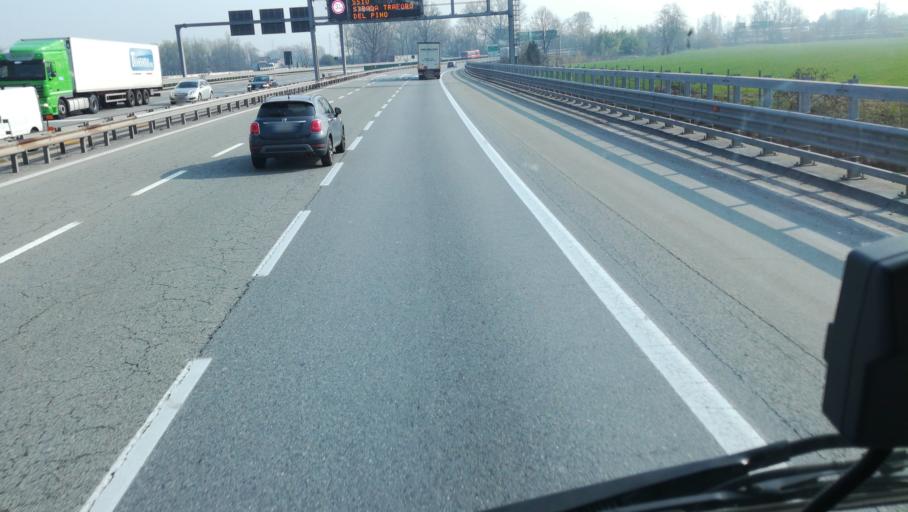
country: IT
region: Piedmont
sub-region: Provincia di Torino
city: Settimo Torinese
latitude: 45.1365
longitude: 7.7198
